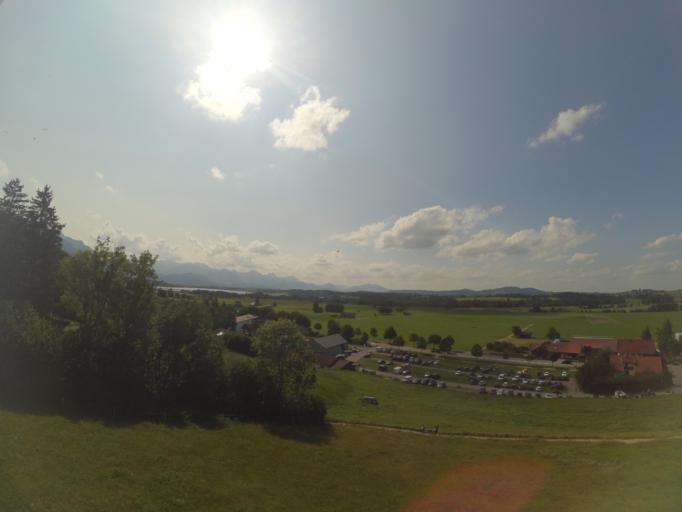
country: DE
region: Bavaria
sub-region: Swabia
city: Halblech
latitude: 47.6135
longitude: 10.8065
